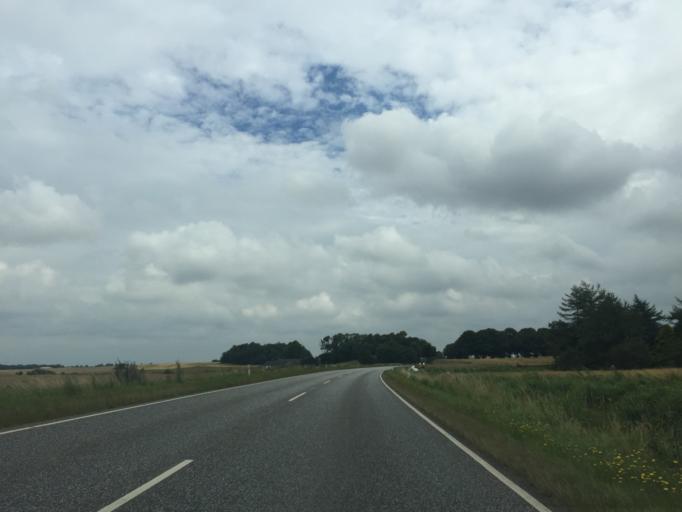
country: DK
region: Central Jutland
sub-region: Randers Kommune
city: Langa
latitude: 56.3752
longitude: 9.9436
